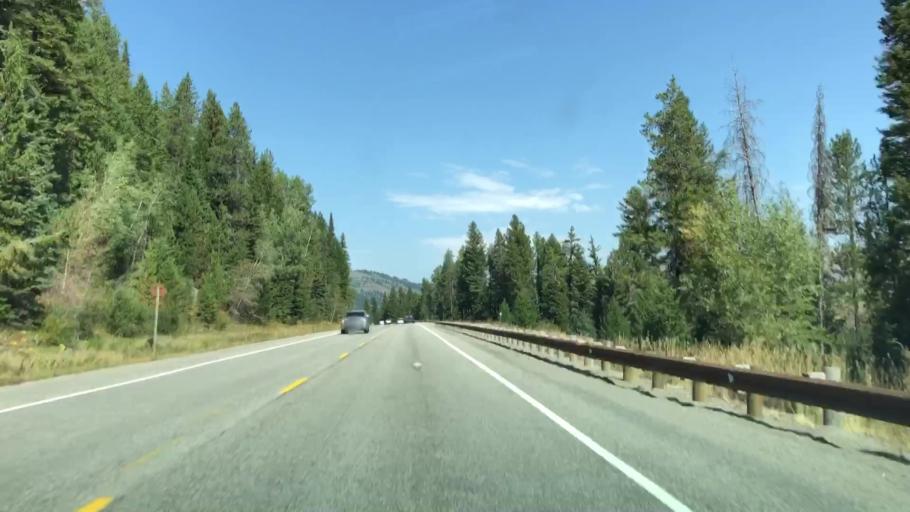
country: US
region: Wyoming
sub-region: Teton County
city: Hoback
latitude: 43.2621
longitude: -110.7832
